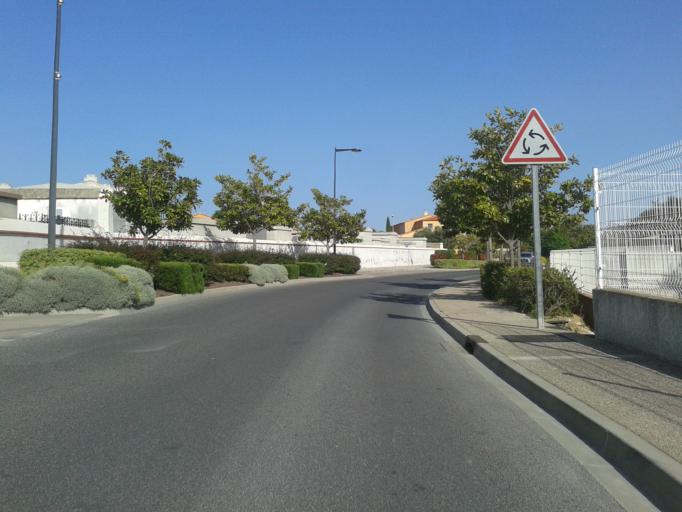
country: FR
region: Languedoc-Roussillon
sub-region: Departement des Pyrenees-Orientales
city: Pezilla-la-Riviere
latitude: 42.6942
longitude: 2.7761
